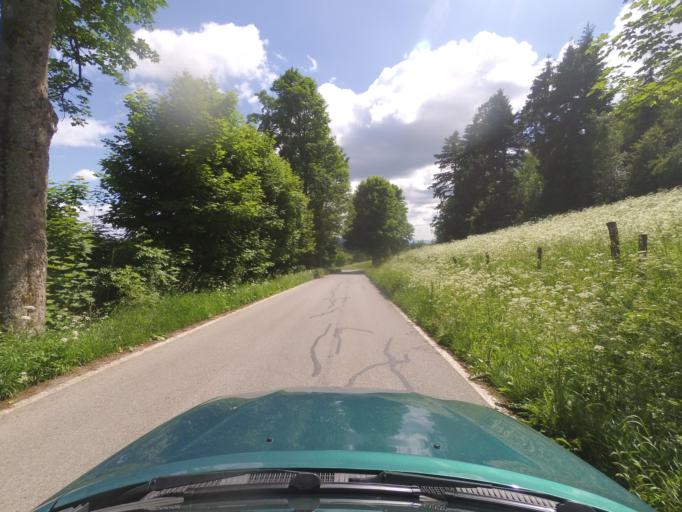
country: PL
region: Lower Silesian Voivodeship
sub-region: Powiat klodzki
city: Miedzylesie
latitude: 50.1166
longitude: 16.6283
